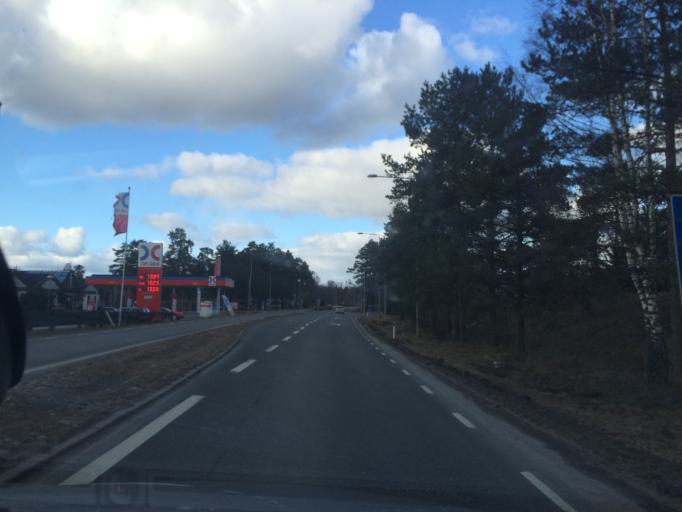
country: SE
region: Joenkoeping
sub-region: Vaggeryds Kommun
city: Skillingaryd
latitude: 57.3490
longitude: 14.0991
